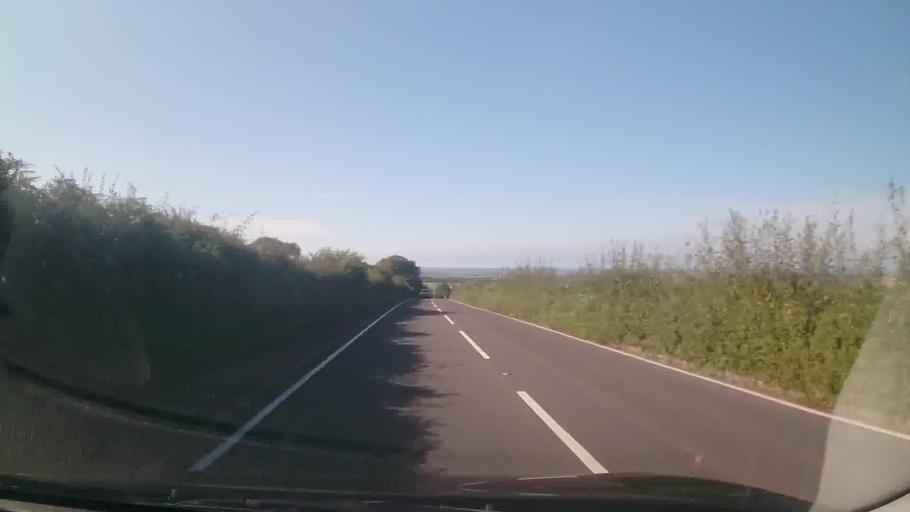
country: GB
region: England
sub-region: Cumbria
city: Seascale
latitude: 54.3304
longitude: -3.3726
